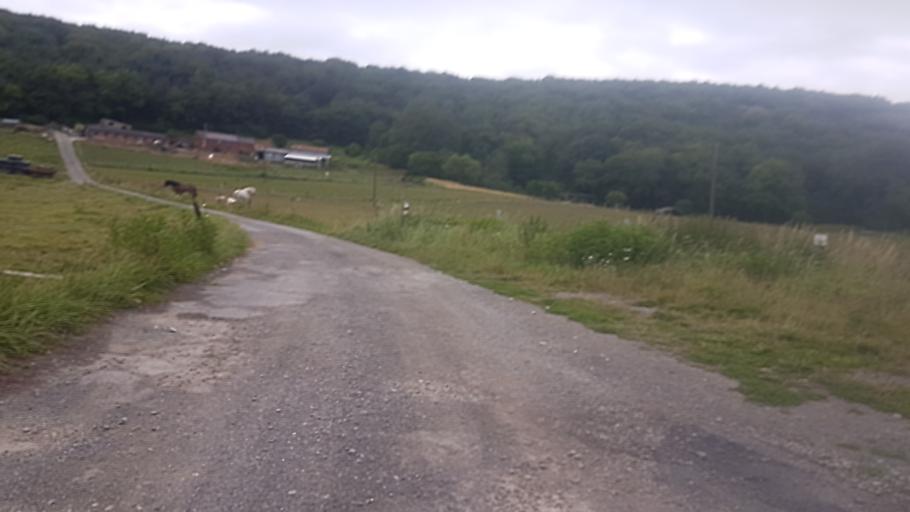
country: BE
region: Wallonia
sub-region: Province de Namur
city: Couvin
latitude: 50.0870
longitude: 4.5561
